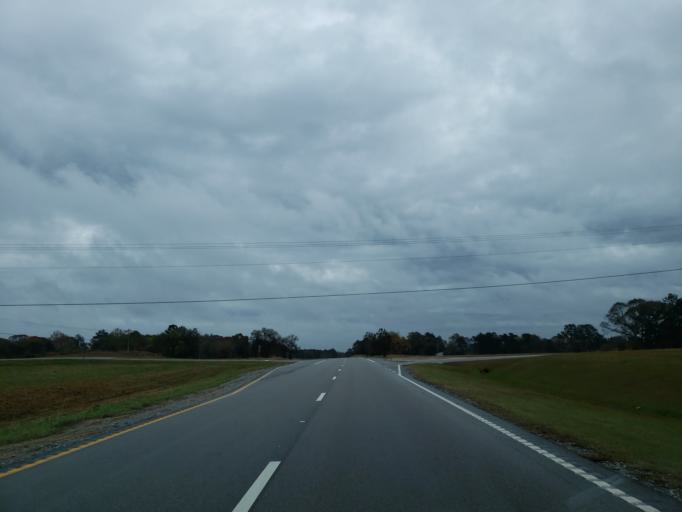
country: US
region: Mississippi
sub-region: Wayne County
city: Waynesboro
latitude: 31.6957
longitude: -88.7323
